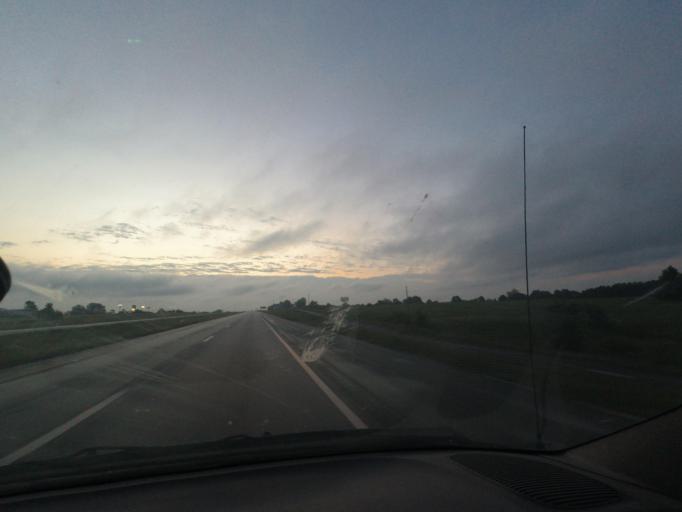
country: US
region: Missouri
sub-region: Linn County
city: Brookfield
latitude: 39.7624
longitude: -93.0136
